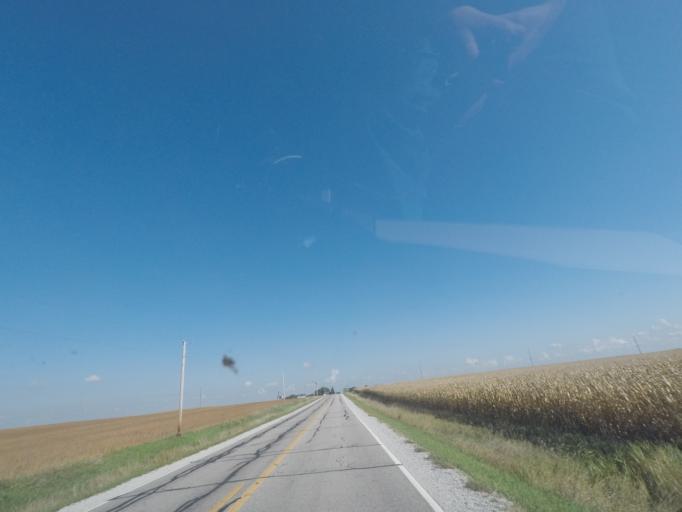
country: US
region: Iowa
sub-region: Story County
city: Nevada
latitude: 42.0322
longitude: -93.4058
